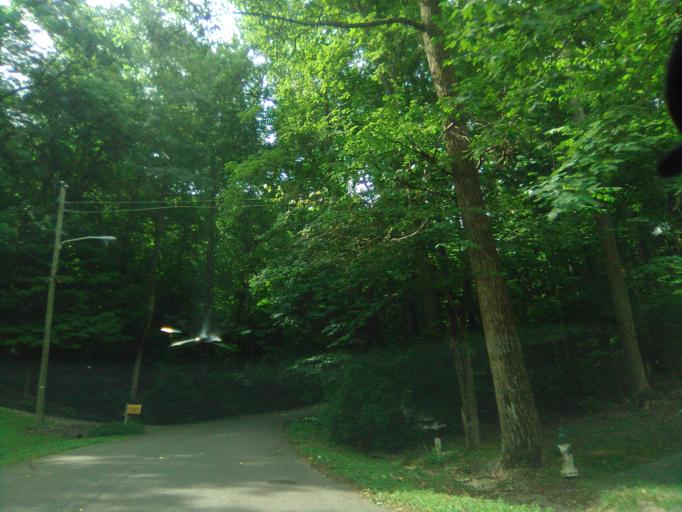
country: US
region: Tennessee
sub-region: Davidson County
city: Belle Meade
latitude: 36.0994
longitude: -86.9074
